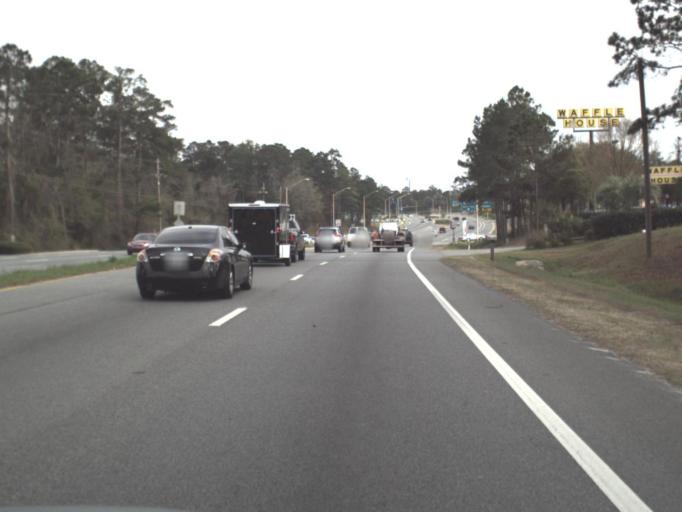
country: US
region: Florida
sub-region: Leon County
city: Tallahassee
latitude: 30.4864
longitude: -84.3155
